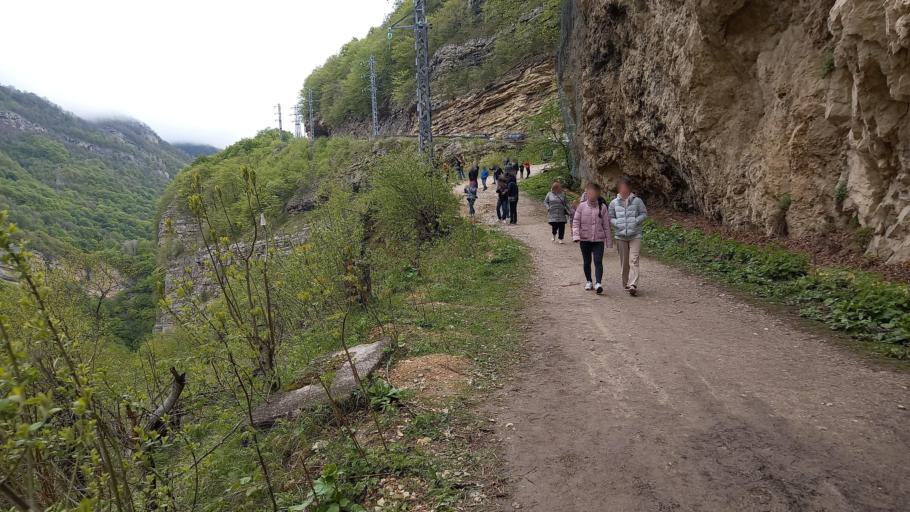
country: RU
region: Kabardino-Balkariya
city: Verkhnyaya Balkariya
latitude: 43.1916
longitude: 43.5176
